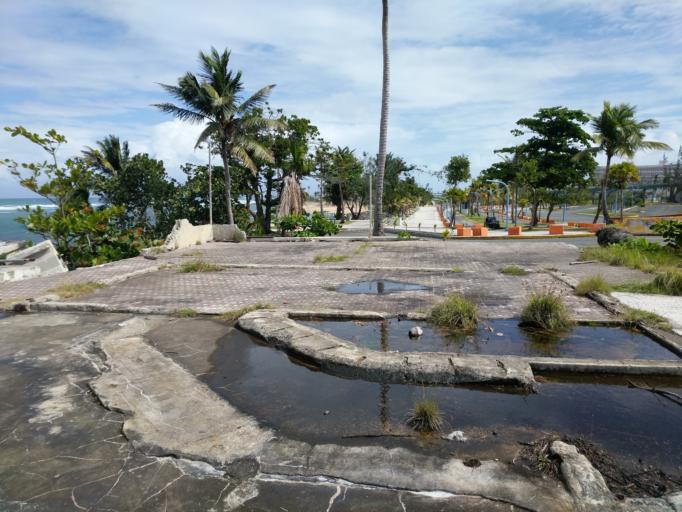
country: PR
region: San Juan
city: San Juan
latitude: 18.4664
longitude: -66.0931
